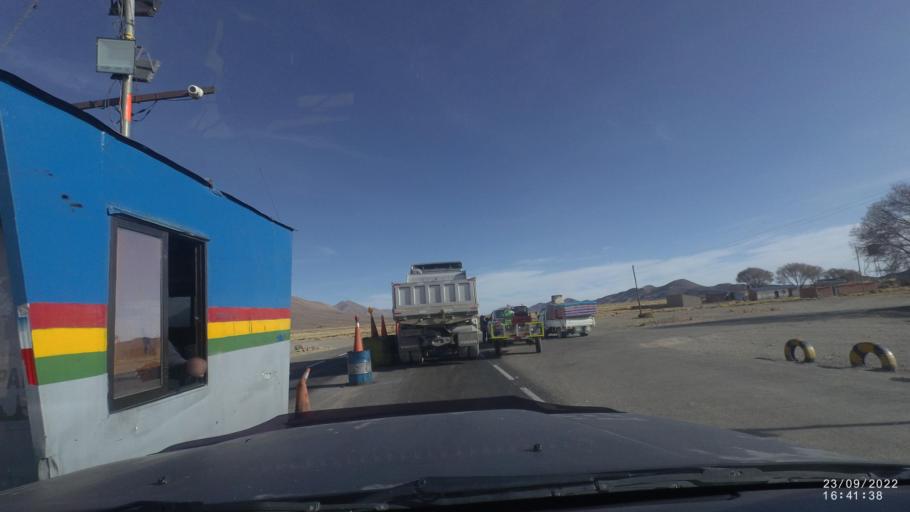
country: BO
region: Oruro
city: Poopo
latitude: -18.2896
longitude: -66.9934
